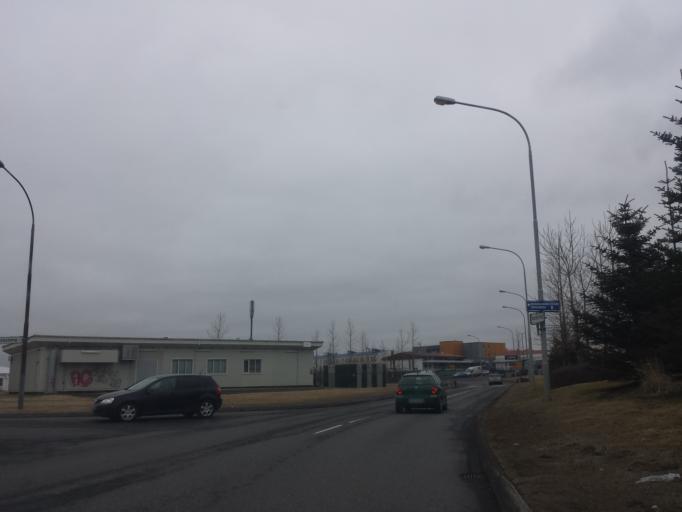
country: IS
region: Capital Region
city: Reykjavik
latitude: 64.1027
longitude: -21.8265
